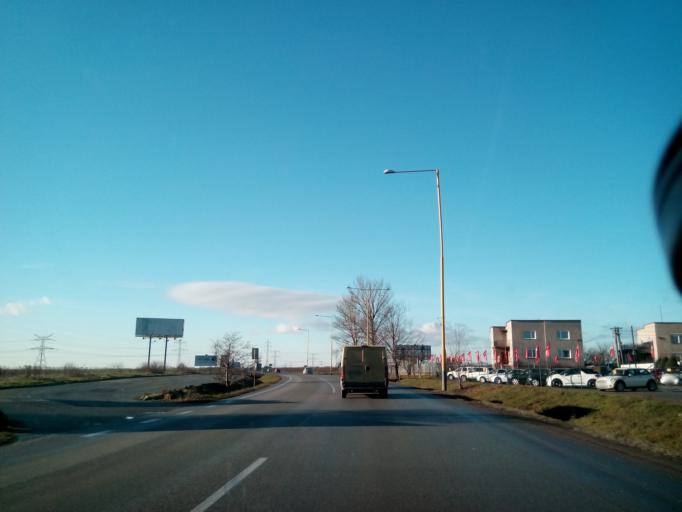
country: SK
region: Kosicky
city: Kosice
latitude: 48.6282
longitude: 21.1652
